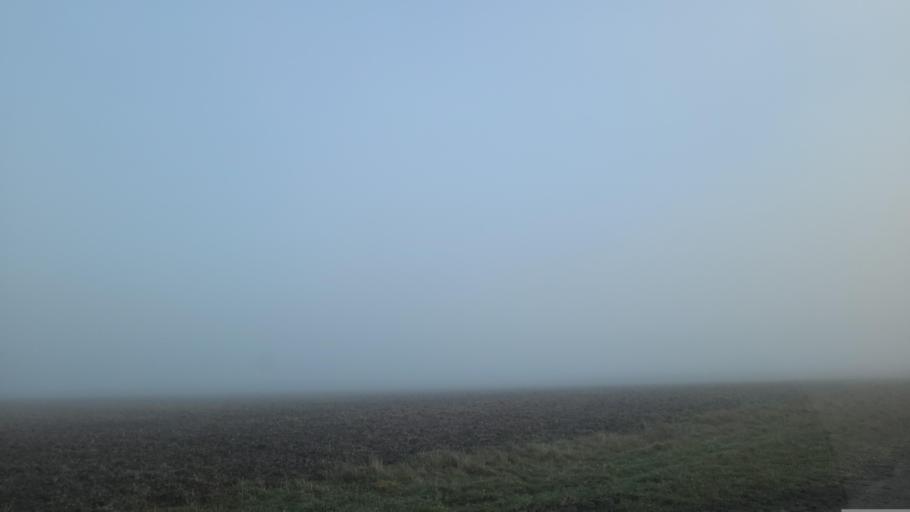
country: SE
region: Uppsala
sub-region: Enkopings Kommun
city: Grillby
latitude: 59.6051
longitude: 17.1708
